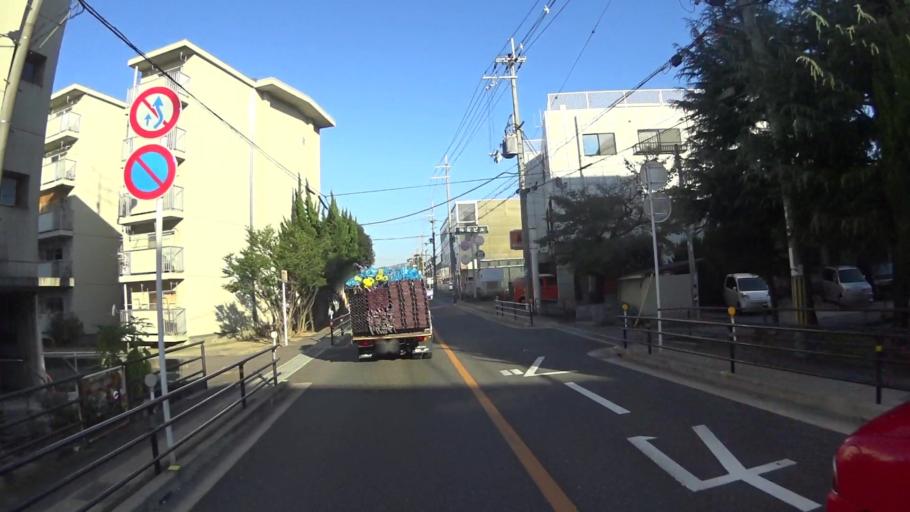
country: JP
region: Kyoto
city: Muko
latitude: 34.9453
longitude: 135.6962
